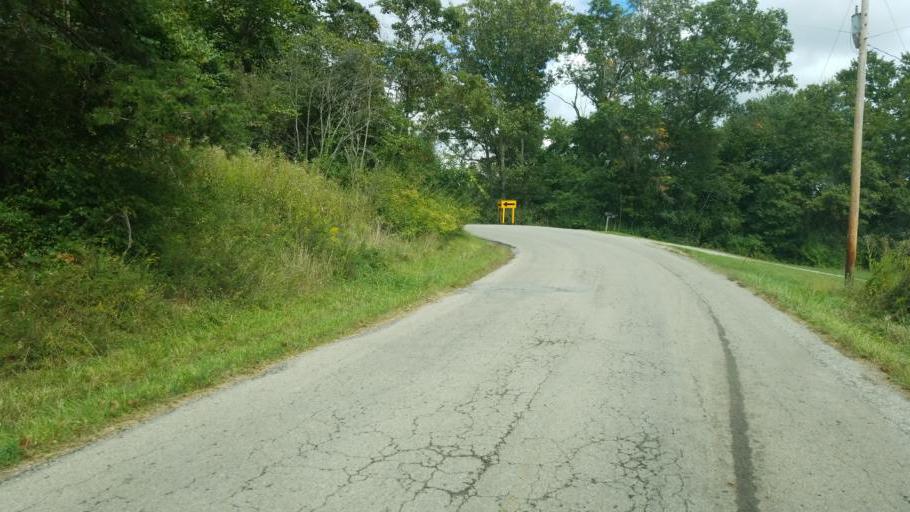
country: US
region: Ohio
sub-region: Jackson County
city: Oak Hill
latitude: 38.8882
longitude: -82.6059
